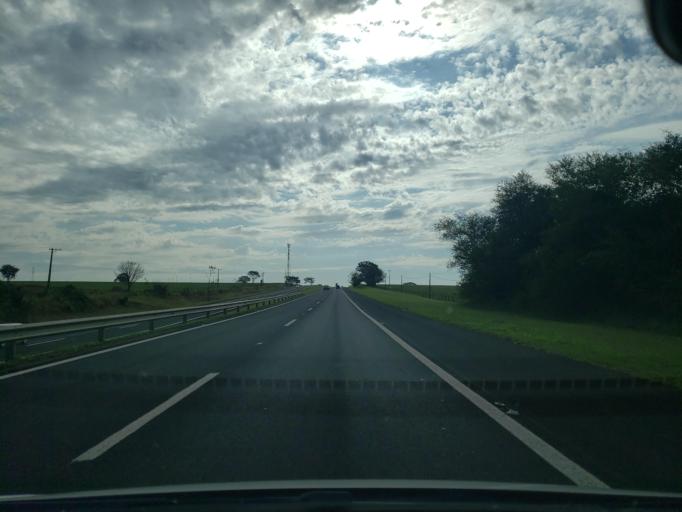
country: BR
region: Sao Paulo
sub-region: Birigui
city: Birigui
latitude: -21.3431
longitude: -50.3208
